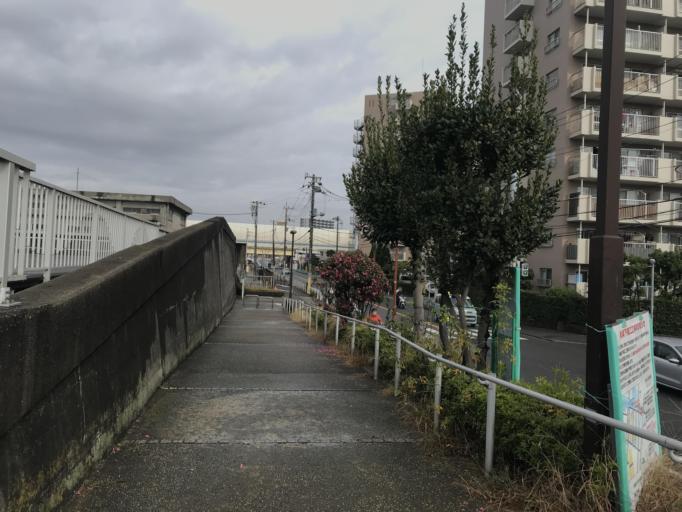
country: JP
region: Chiba
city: Funabashi
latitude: 35.6894
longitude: 139.9880
